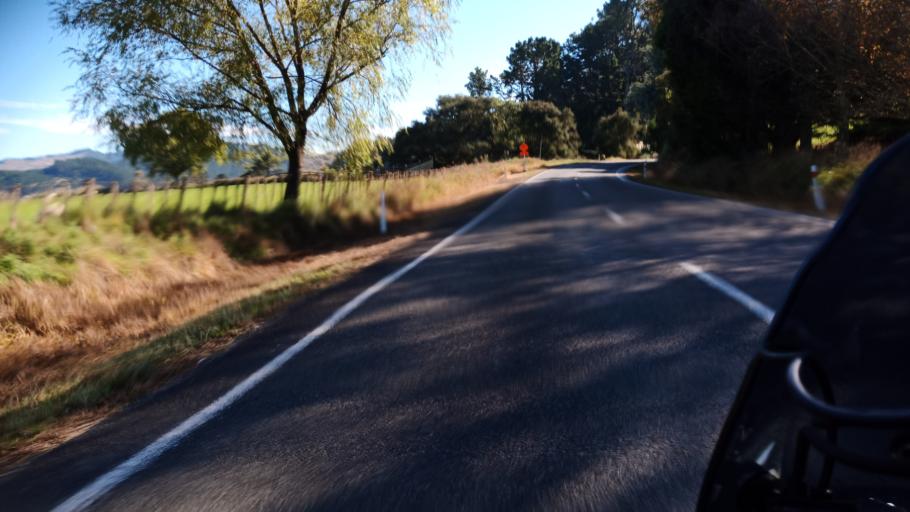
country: NZ
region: Hawke's Bay
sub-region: Wairoa District
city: Wairoa
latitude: -38.9291
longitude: 177.2742
